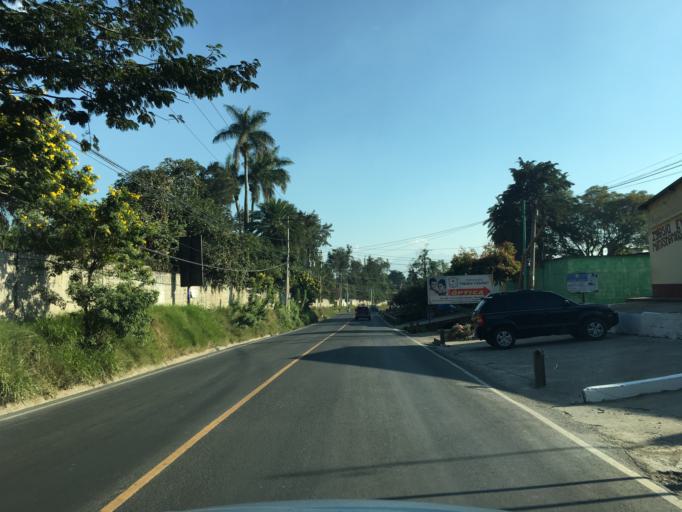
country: GT
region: Guatemala
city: Villa Nueva
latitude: 14.5399
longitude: -90.6153
